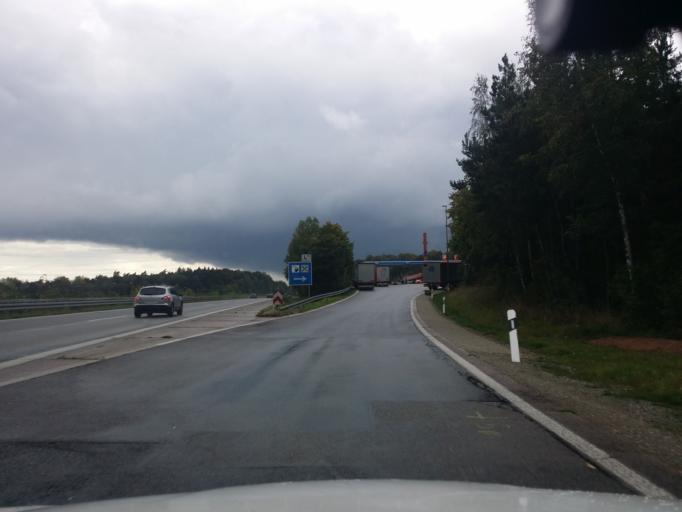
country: DE
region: Hesse
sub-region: Regierungsbezirk Kassel
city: Burghaun
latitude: 50.7118
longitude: 9.6643
